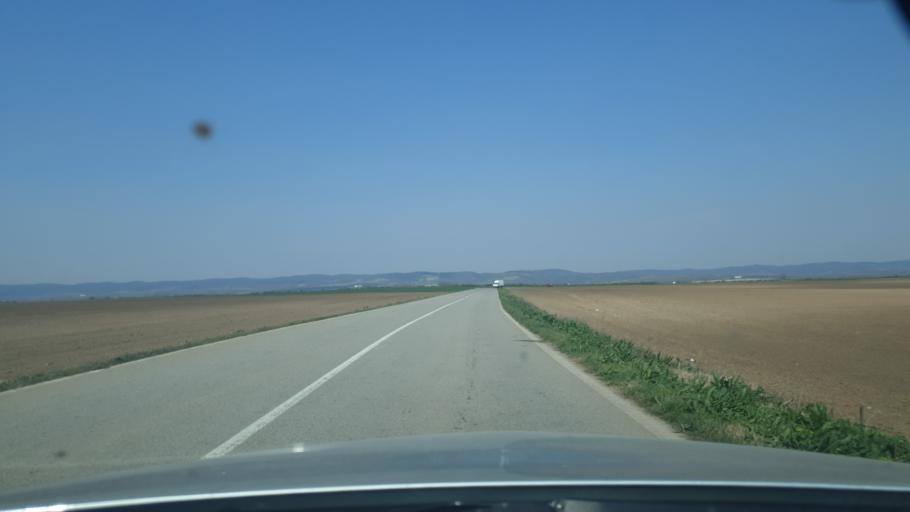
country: RS
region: Autonomna Pokrajina Vojvodina
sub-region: Sremski Okrug
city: Ruma
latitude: 45.0416
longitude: 19.7609
